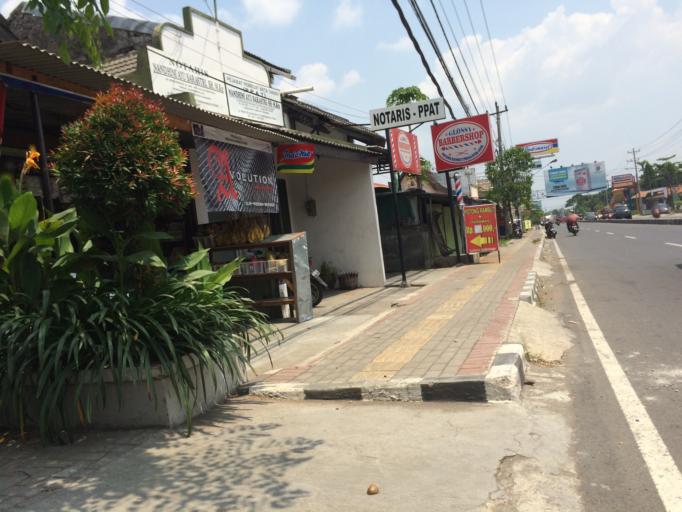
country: ID
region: Central Java
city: Grogol
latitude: -7.6190
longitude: 110.8206
